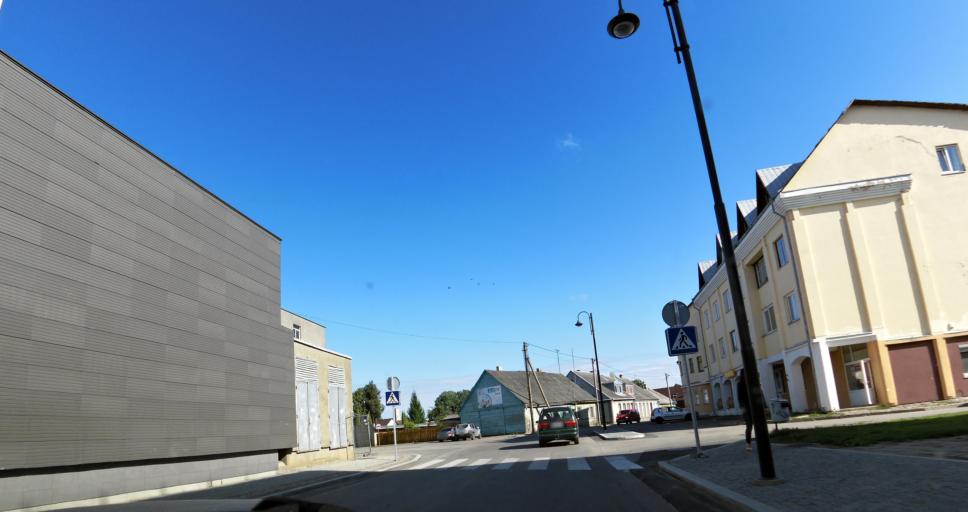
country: LT
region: Panevezys
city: Pasvalys
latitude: 56.0620
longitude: 24.4004
